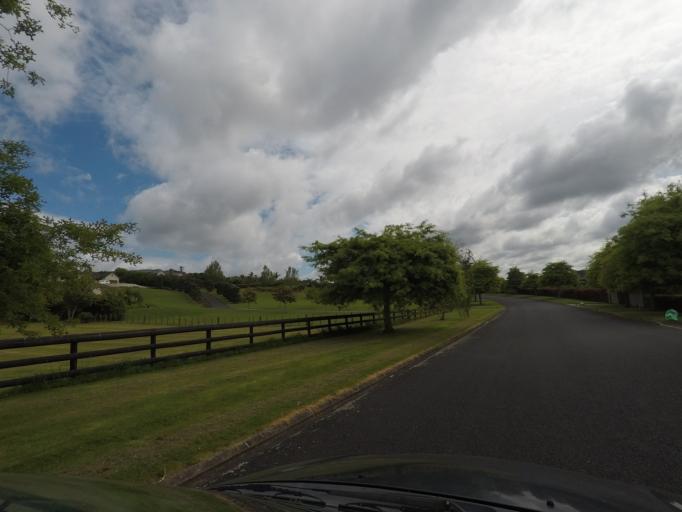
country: NZ
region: Auckland
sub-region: Auckland
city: Muriwai Beach
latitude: -36.7673
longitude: 174.5704
